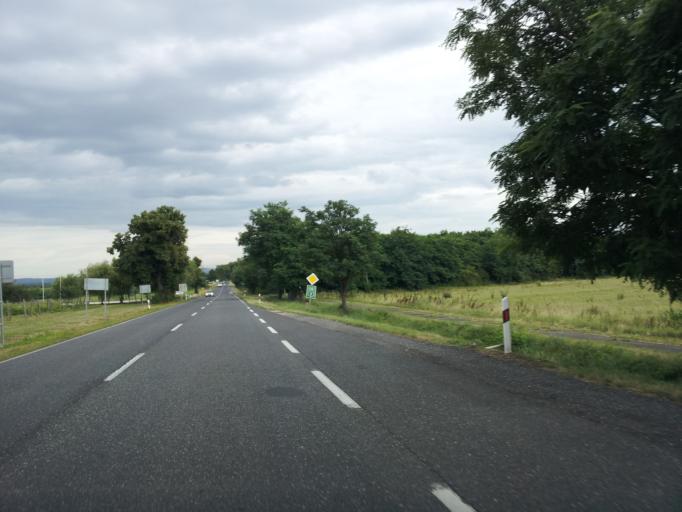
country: HU
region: Veszprem
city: Devecser
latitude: 47.1276
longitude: 17.3602
